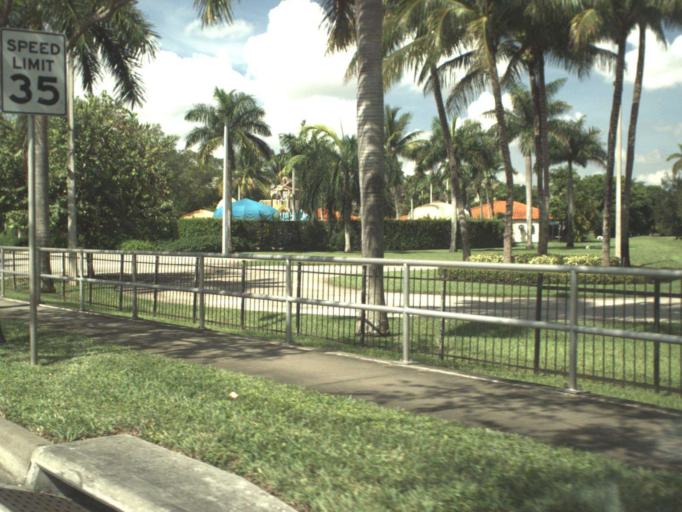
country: US
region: Florida
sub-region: Miami-Dade County
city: Biscayne Park
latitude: 25.8703
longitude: -80.1741
